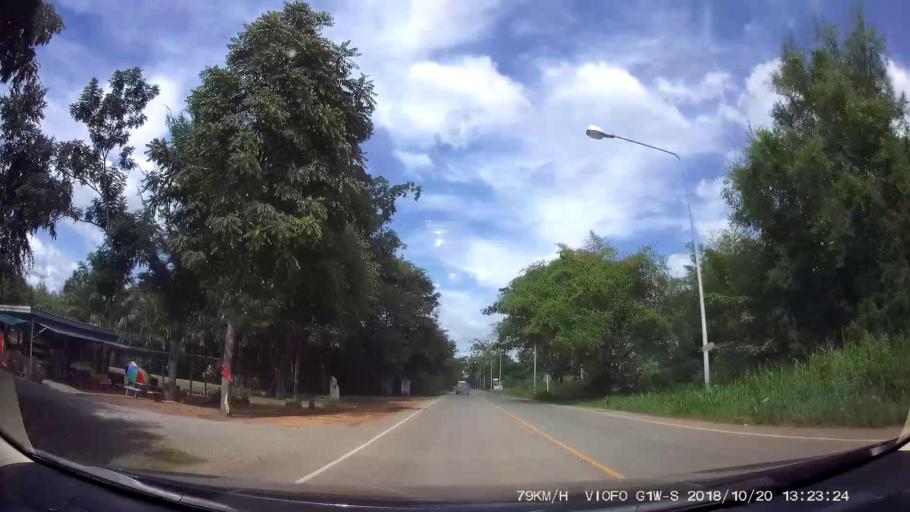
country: TH
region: Chaiyaphum
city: Khon San
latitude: 16.5831
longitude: 101.9213
